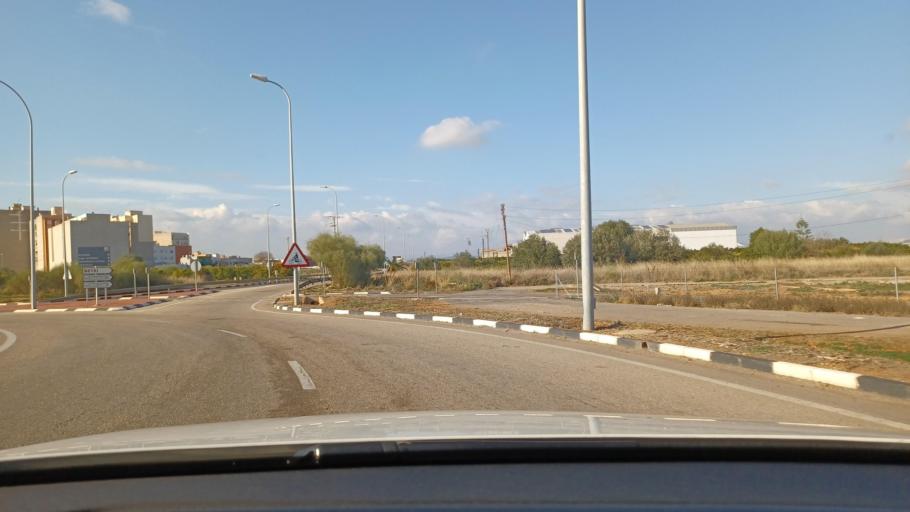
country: ES
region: Valencia
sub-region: Provincia de Castello
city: Betxi
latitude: 39.9273
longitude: -0.1917
